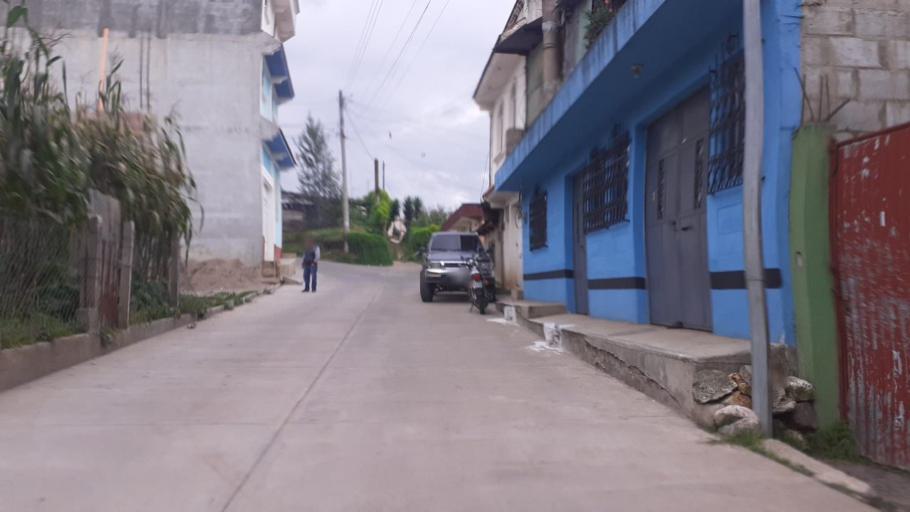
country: GT
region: Quetzaltenango
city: Ostuncalco
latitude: 14.8720
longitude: -91.6187
